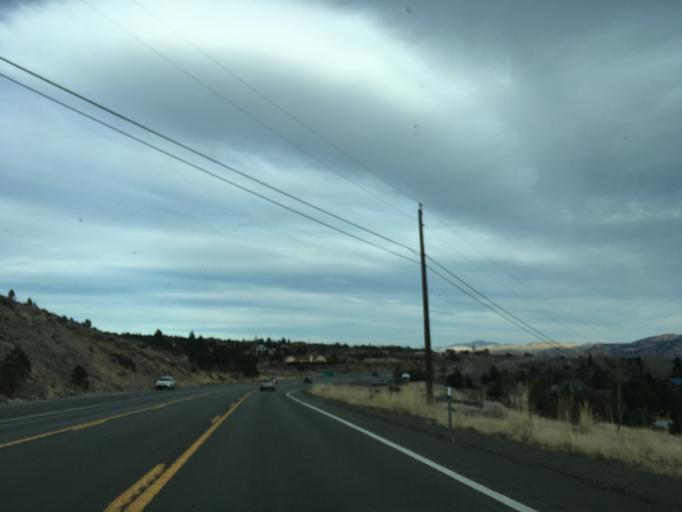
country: US
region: Nevada
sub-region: Washoe County
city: Reno
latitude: 39.3744
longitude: -119.8420
